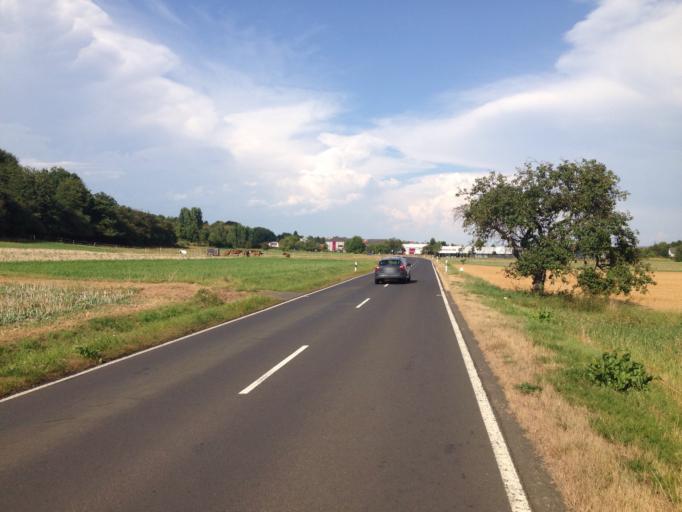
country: DE
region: Hesse
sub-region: Regierungsbezirk Giessen
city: Giessen
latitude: 50.6145
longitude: 8.6589
